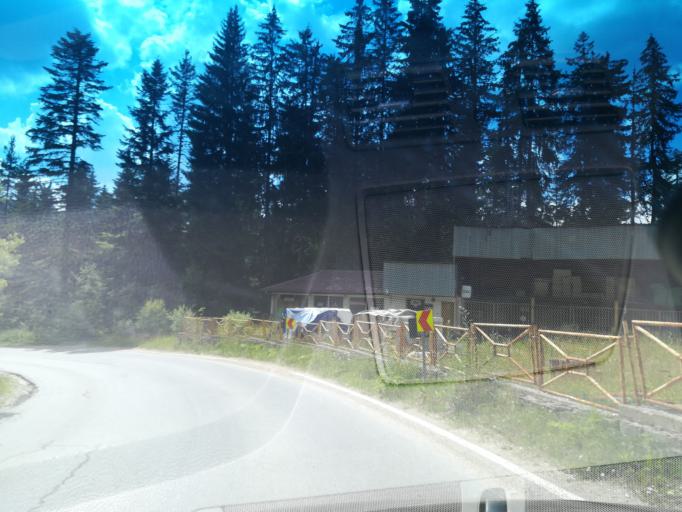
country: BG
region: Smolyan
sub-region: Obshtina Smolyan
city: Smolyan
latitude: 41.6521
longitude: 24.6924
